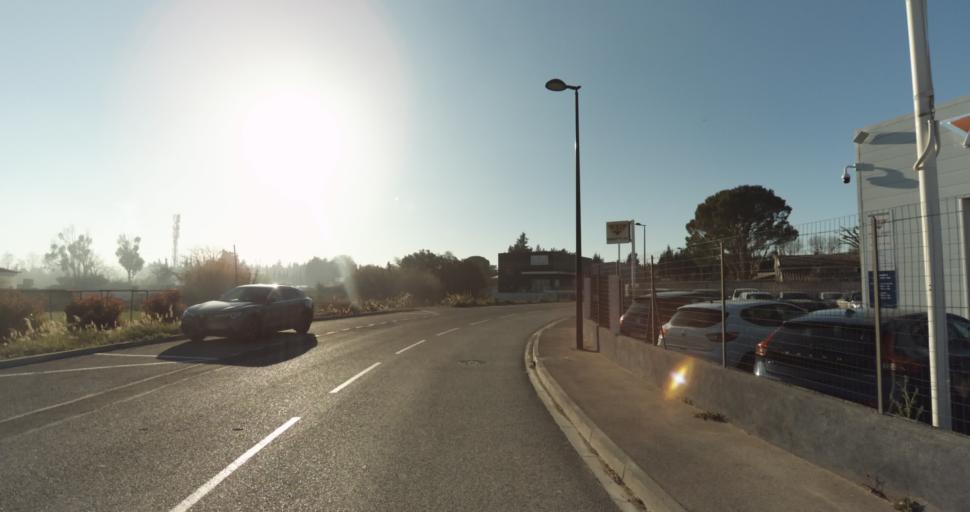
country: FR
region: Provence-Alpes-Cote d'Azur
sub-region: Departement des Bouches-du-Rhone
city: Pelissanne
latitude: 43.6298
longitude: 5.1394
